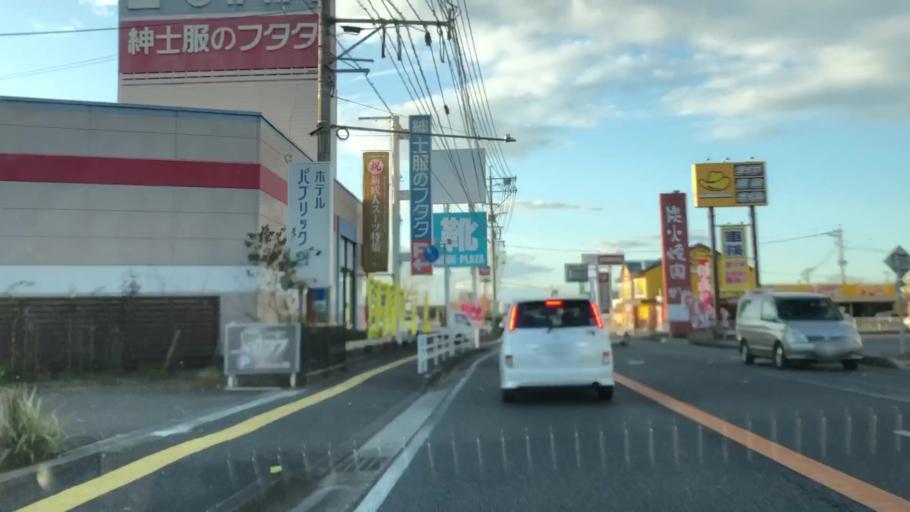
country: JP
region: Oita
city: Bungo-Takada-shi
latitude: 33.5290
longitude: 131.3383
